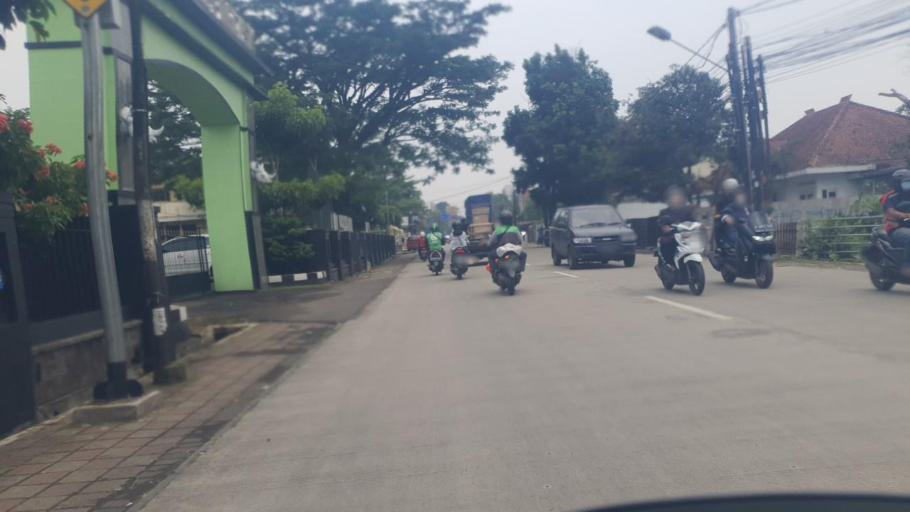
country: ID
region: West Java
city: Bogor
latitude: -6.5872
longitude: 106.7877
